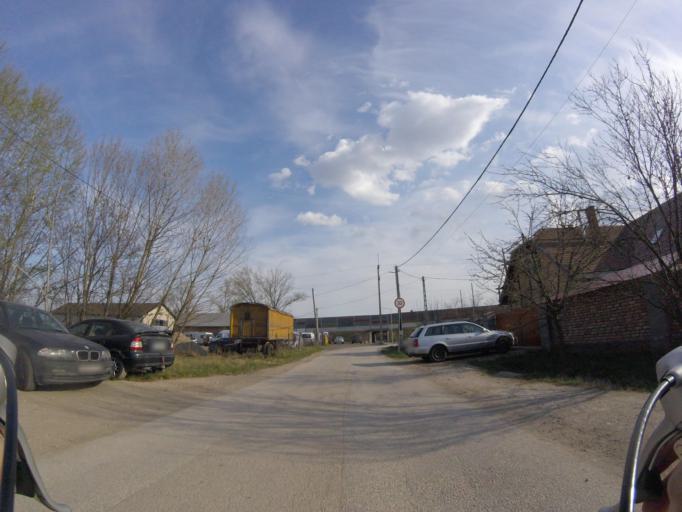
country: HU
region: Pest
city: Diosd
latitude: 47.3974
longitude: 18.9481
